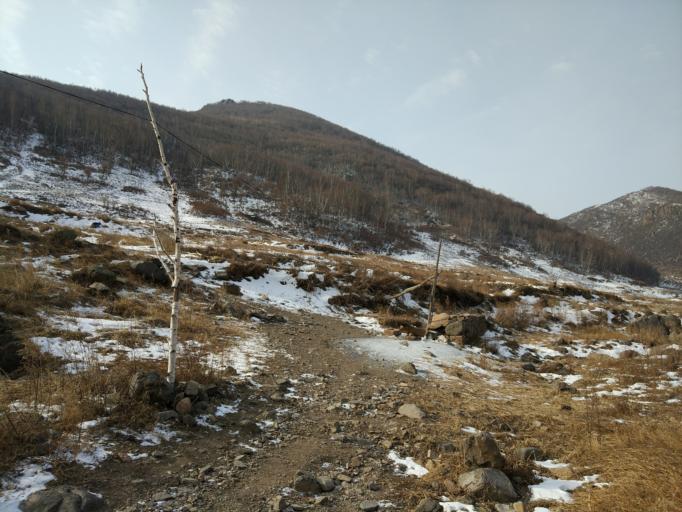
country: CN
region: Hebei
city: Xiwanzi
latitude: 40.8535
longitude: 115.4629
